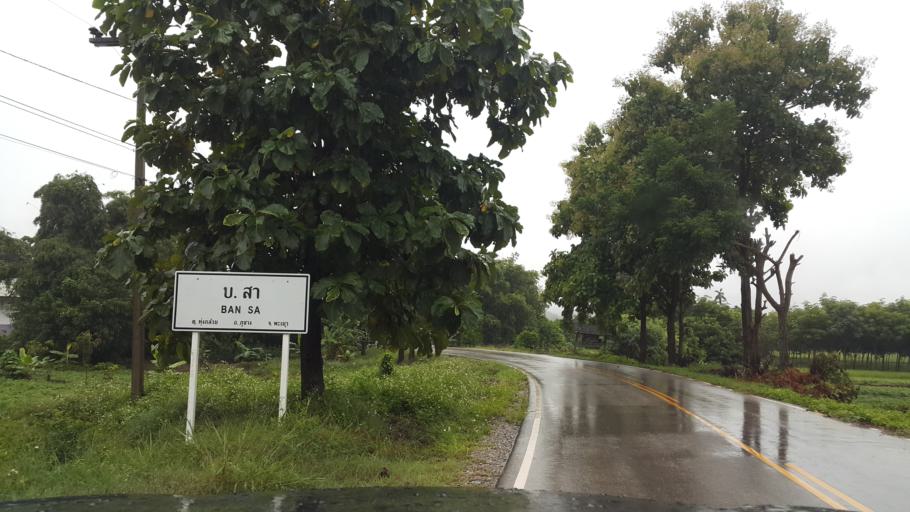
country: TH
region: Phayao
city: Phu Sang
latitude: 19.5983
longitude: 100.3960
